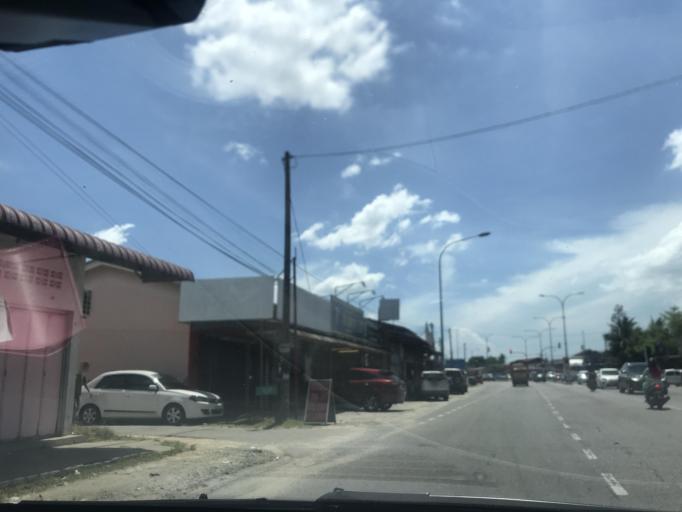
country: MY
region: Kelantan
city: Kota Bharu
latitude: 6.1146
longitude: 102.2672
